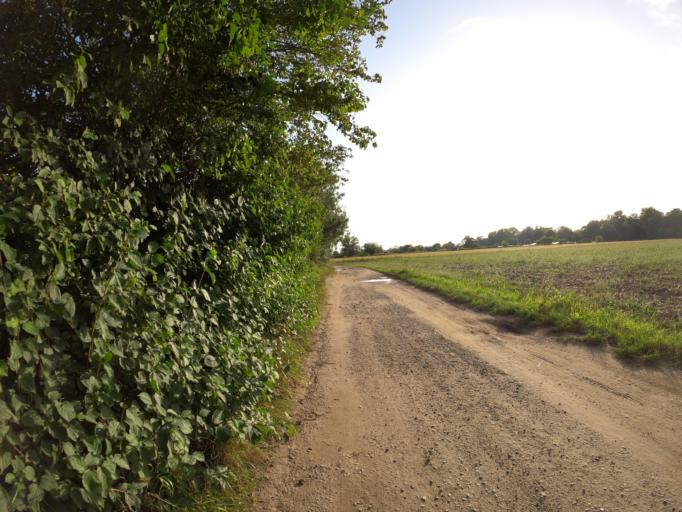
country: FR
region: Midi-Pyrenees
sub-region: Departement de la Haute-Garonne
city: Portet-sur-Garonne
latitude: 43.5411
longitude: 1.4238
